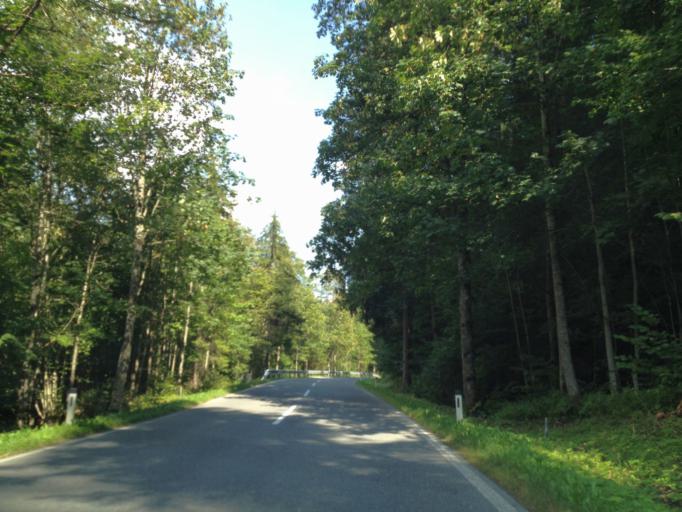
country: AT
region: Styria
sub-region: Politischer Bezirk Liezen
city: Haus
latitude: 47.4175
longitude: 13.7332
